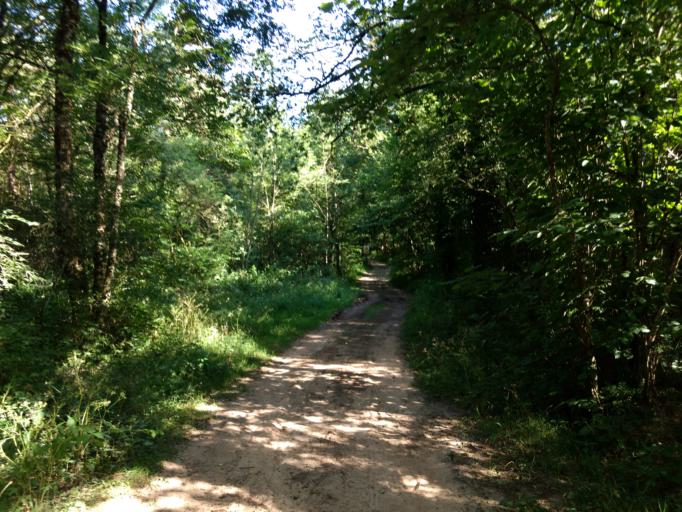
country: FR
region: Midi-Pyrenees
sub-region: Departement de l'Aveyron
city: La Loubiere
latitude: 44.3604
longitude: 2.6943
